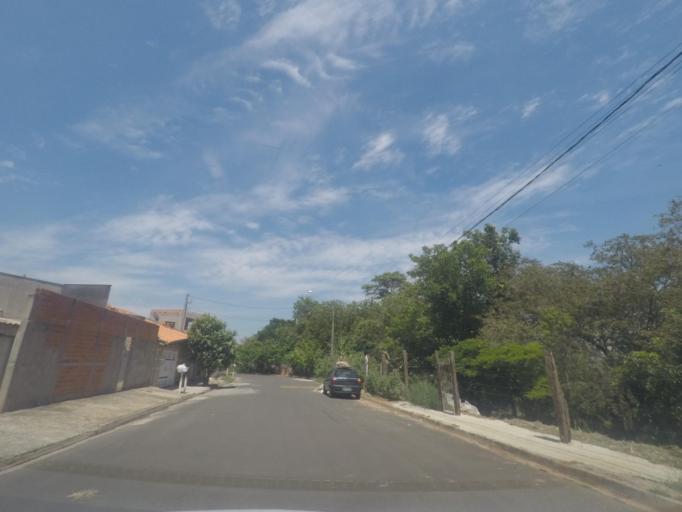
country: BR
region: Sao Paulo
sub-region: Sumare
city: Sumare
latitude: -22.7970
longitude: -47.2667
